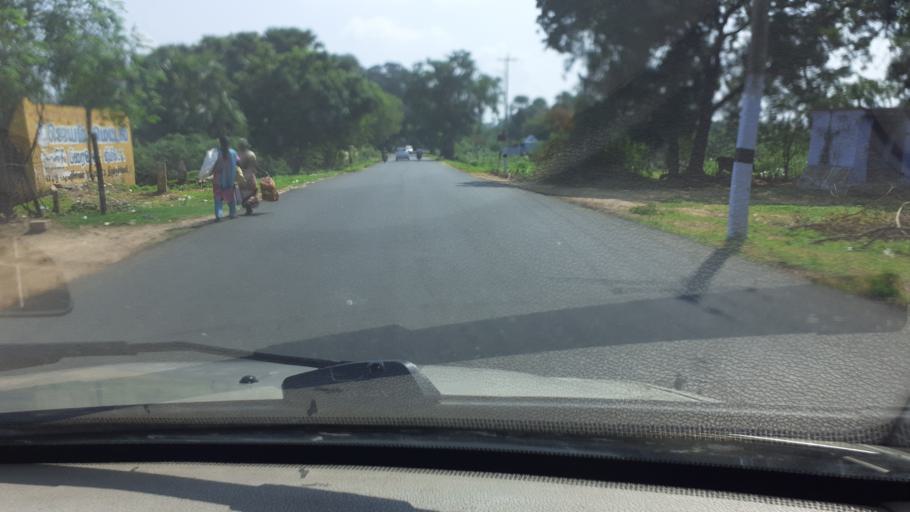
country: IN
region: Tamil Nadu
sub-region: Thoothukkudi
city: Srivaikuntam
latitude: 8.6321
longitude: 77.9008
